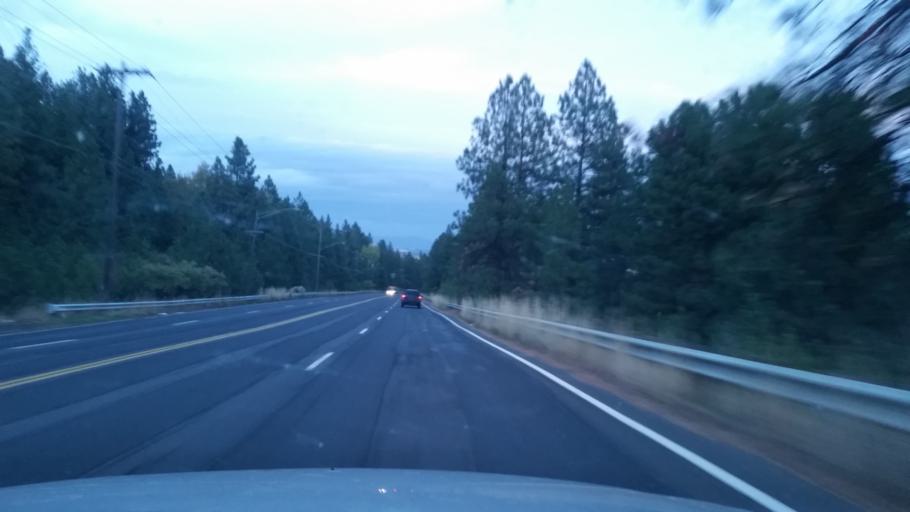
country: US
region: Washington
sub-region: Spokane County
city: Spokane
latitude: 47.6414
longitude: -117.4694
